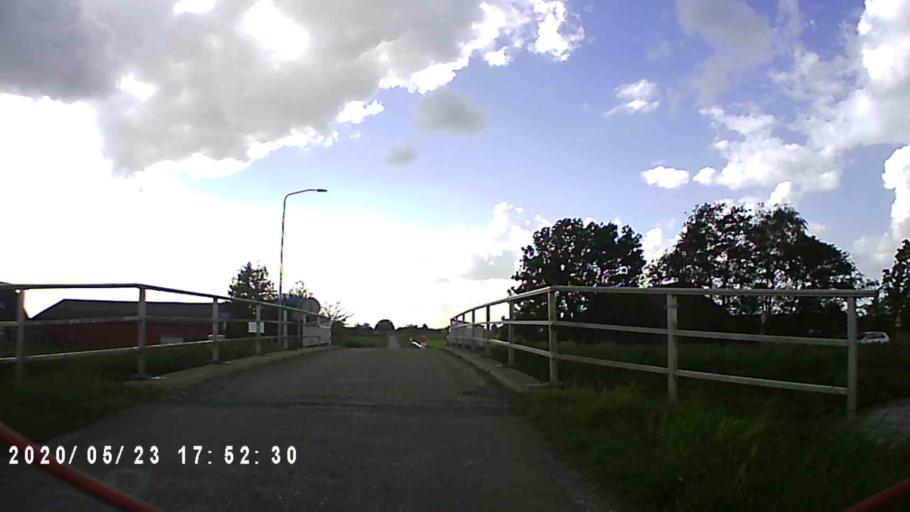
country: NL
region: Groningen
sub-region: Gemeente Slochteren
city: Slochteren
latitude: 53.2431
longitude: 6.7571
